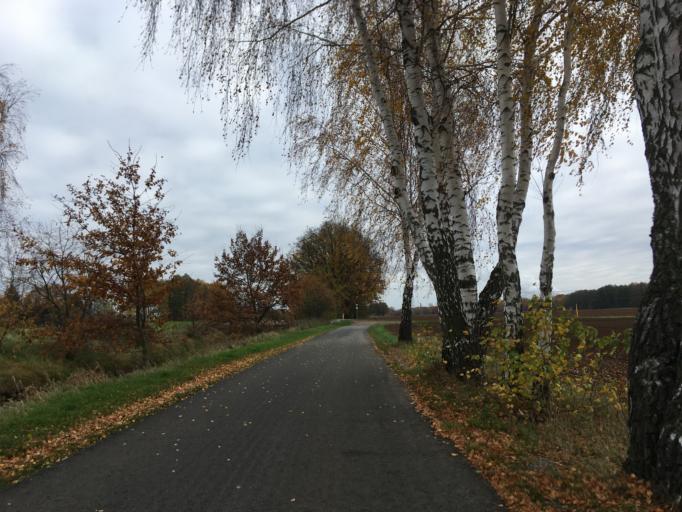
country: DE
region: Brandenburg
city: Drehnow
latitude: 51.8603
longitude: 14.3812
